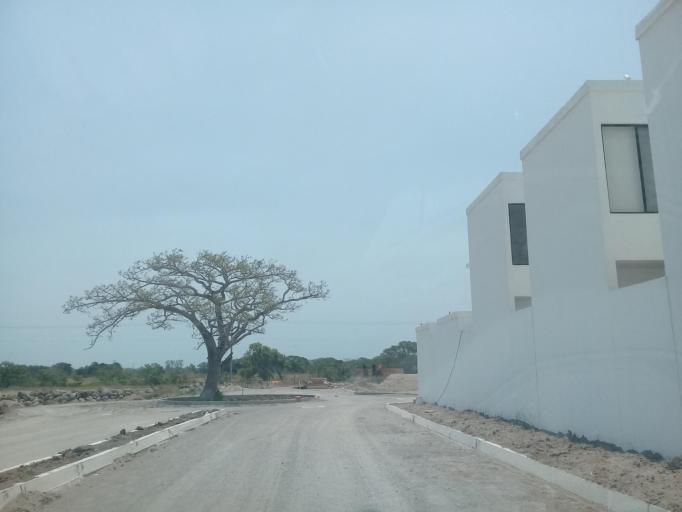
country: MX
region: Veracruz
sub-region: Veracruz
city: Hacienda Sotavento
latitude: 19.1430
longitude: -96.1735
